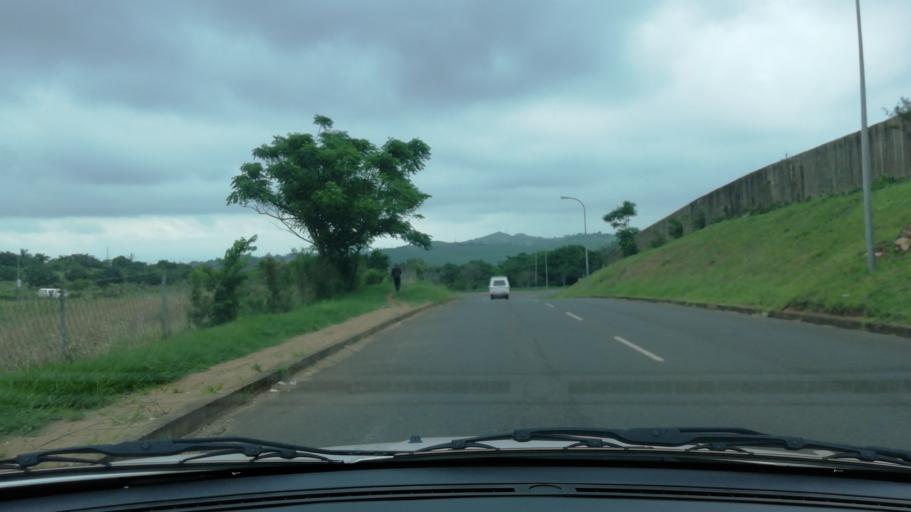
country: ZA
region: KwaZulu-Natal
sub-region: uThungulu District Municipality
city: Empangeni
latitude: -28.7473
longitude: 31.8864
